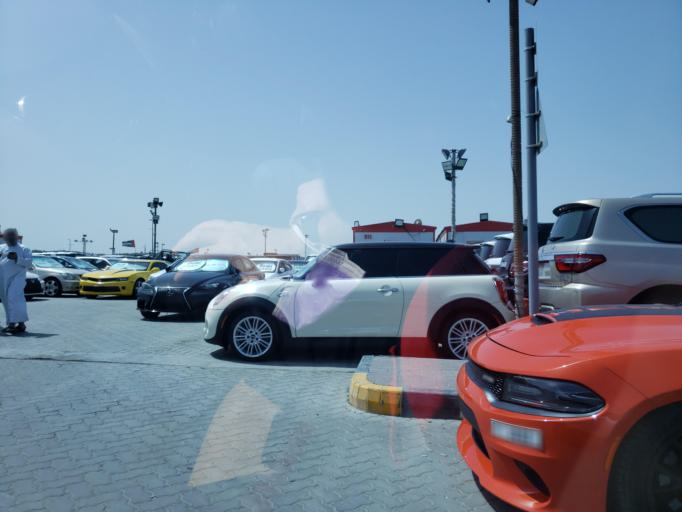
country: AE
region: Ash Shariqah
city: Sharjah
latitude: 25.3413
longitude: 55.4772
